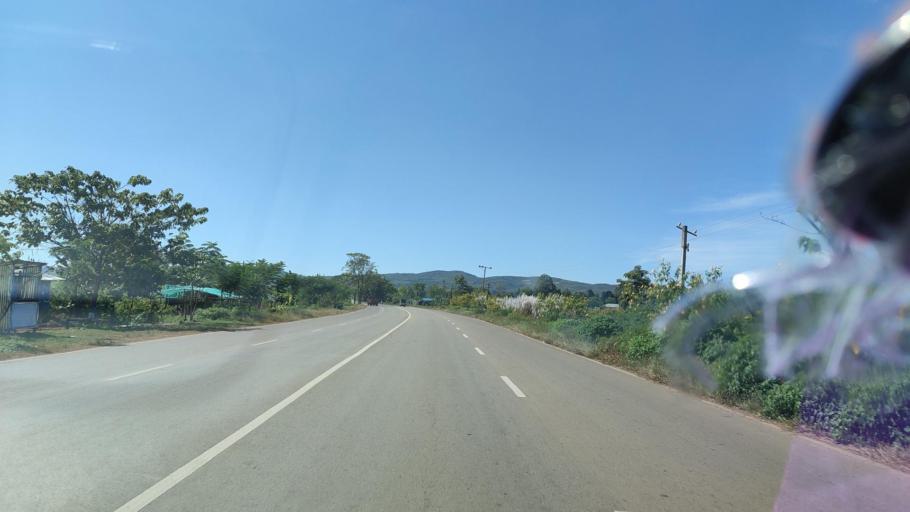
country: MM
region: Shan
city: Taunggyi
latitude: 20.7236
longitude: 96.7824
